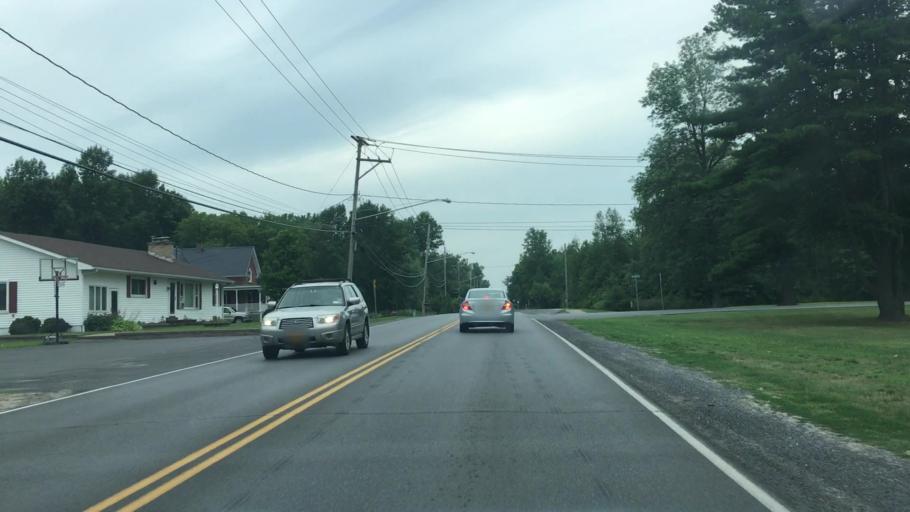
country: US
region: New York
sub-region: Clinton County
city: Plattsburgh West
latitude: 44.6864
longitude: -73.4981
